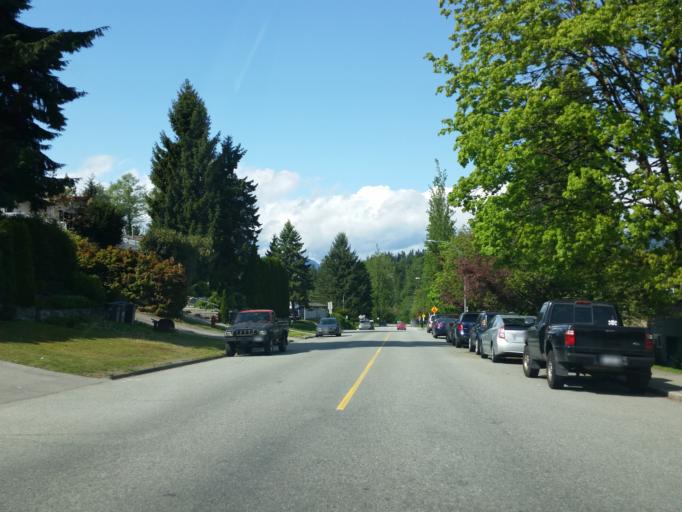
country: CA
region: British Columbia
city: Port Moody
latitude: 49.2770
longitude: -122.8755
